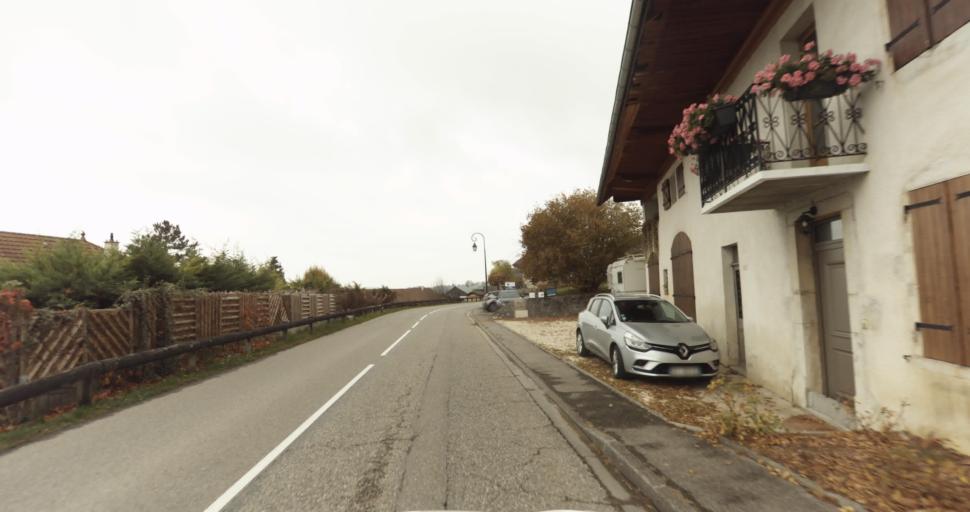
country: FR
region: Rhone-Alpes
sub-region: Departement de la Haute-Savoie
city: Gruffy
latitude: 45.7920
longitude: 6.0555
